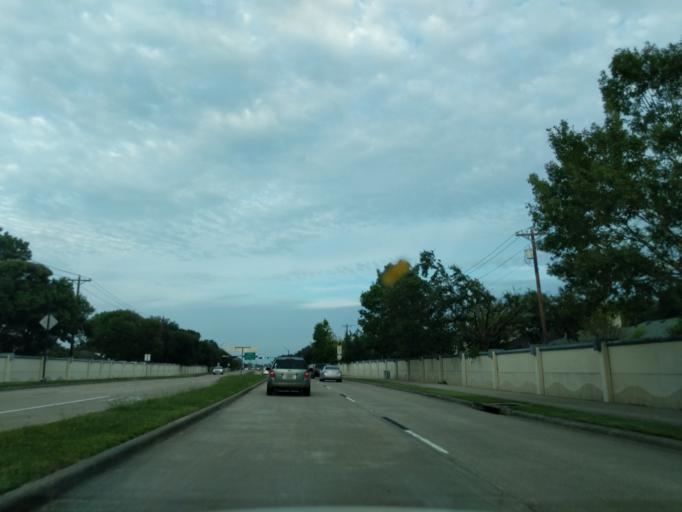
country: US
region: Texas
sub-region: Galveston County
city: Clear Lake Shores
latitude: 29.5267
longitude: -95.0452
